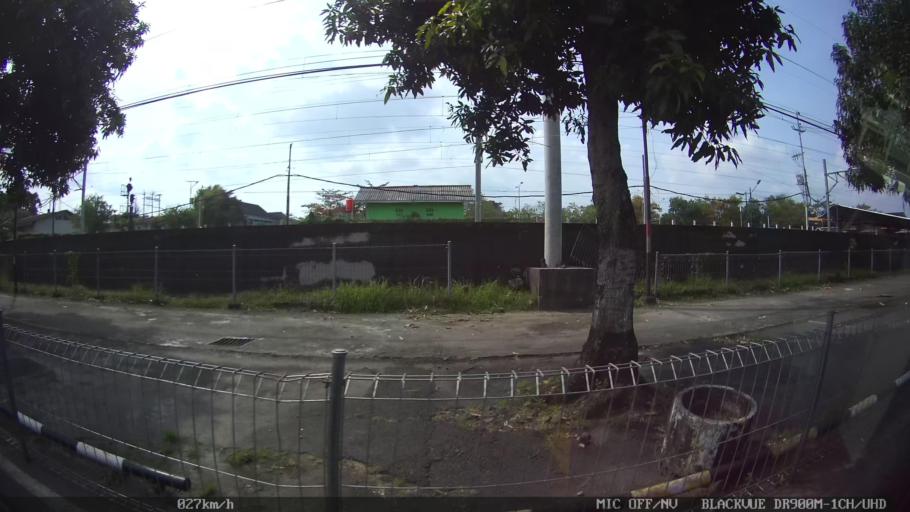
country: ID
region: Daerah Istimewa Yogyakarta
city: Depok
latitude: -7.7855
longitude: 110.4354
